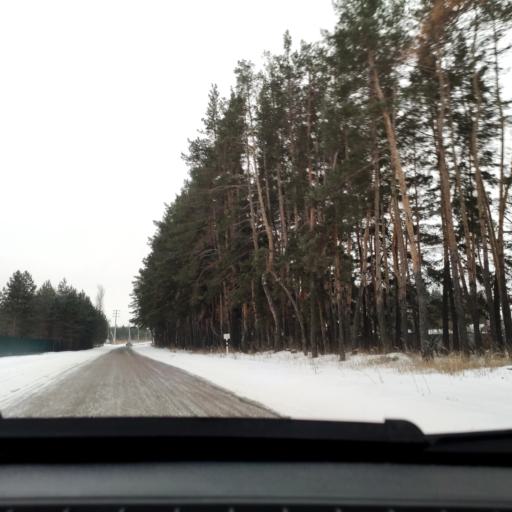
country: RU
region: Voronezj
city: Podgornoye
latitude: 51.8478
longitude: 39.1911
